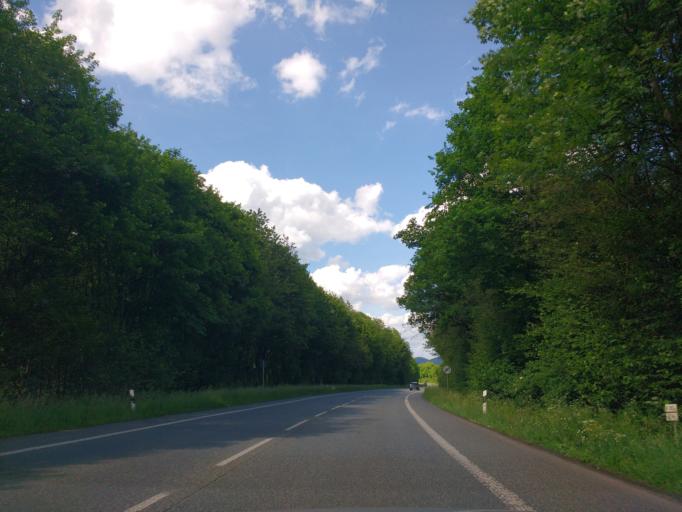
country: DE
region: Hesse
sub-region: Regierungsbezirk Giessen
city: Breidenbach
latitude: 50.9014
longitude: 8.4505
